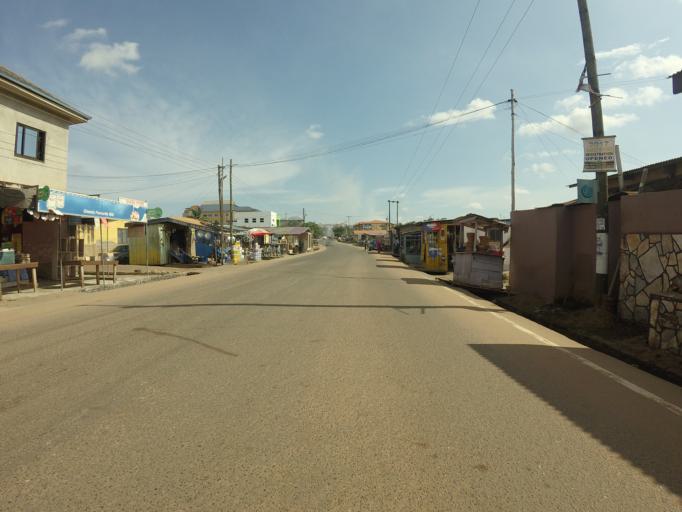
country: GH
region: Greater Accra
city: Medina Estates
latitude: 5.6743
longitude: -0.1820
